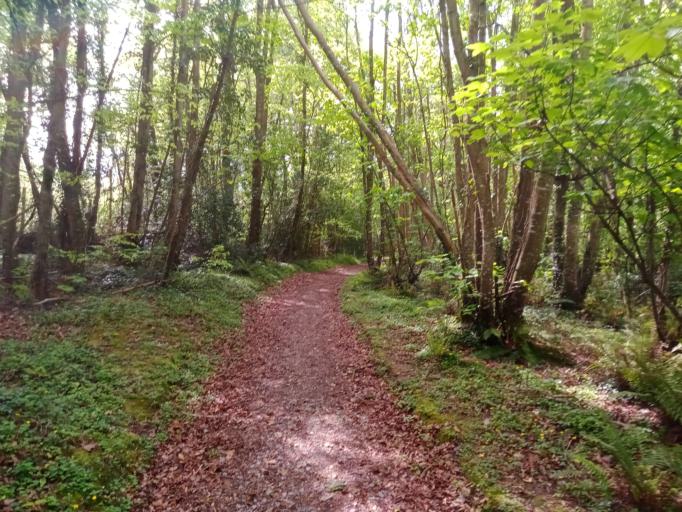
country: IE
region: Leinster
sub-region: Kilkenny
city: Ballyragget
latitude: 52.7217
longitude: -7.4046
